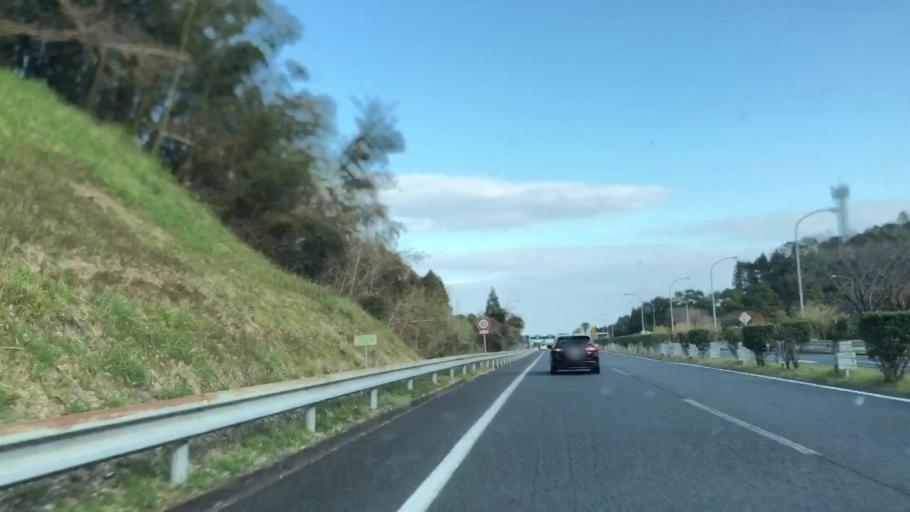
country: JP
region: Miyazaki
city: Miyazaki-shi
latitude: 31.8674
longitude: 131.3946
